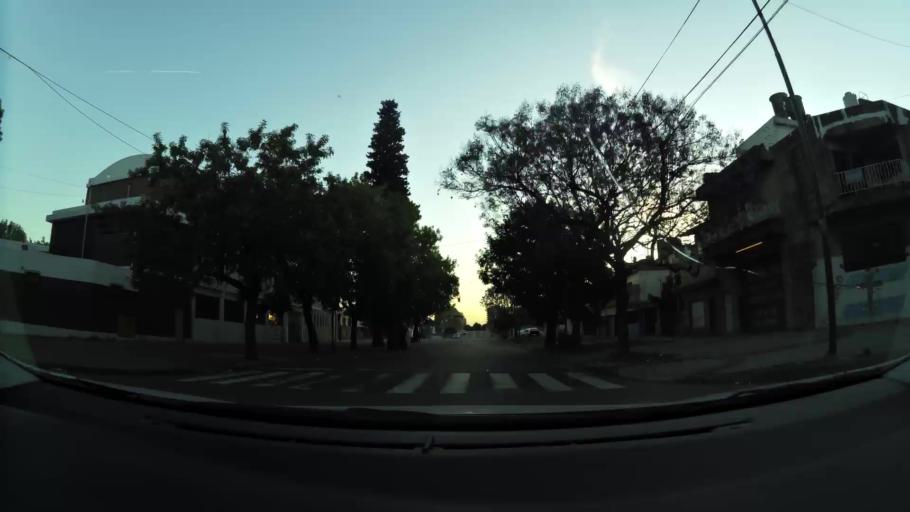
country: AR
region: Buenos Aires F.D.
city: Villa Lugano
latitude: -34.6717
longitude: -58.4694
